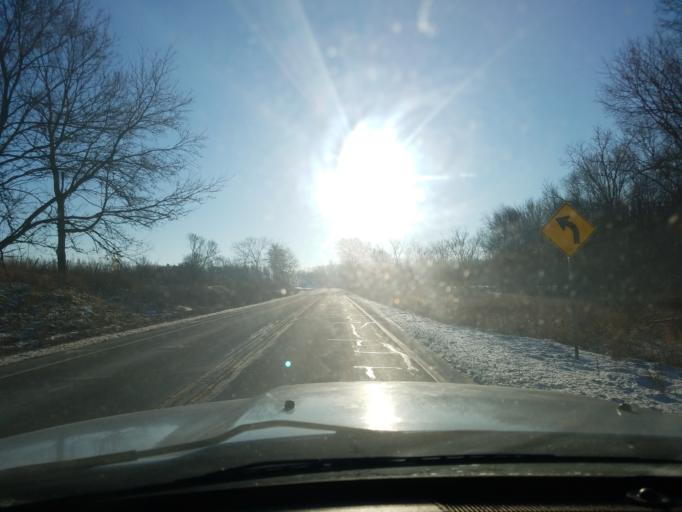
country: US
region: Indiana
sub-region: Noble County
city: Ligonier
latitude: 41.4589
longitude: -85.5118
